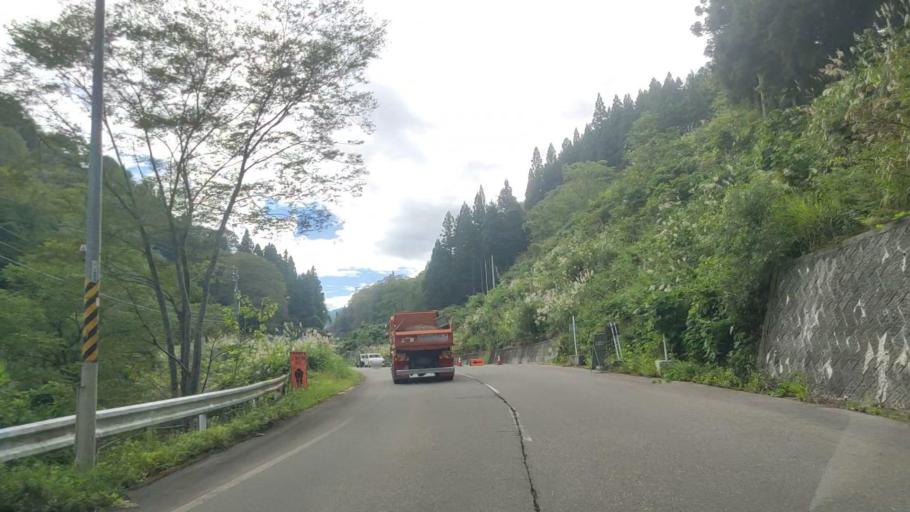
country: JP
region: Nagano
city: Iiyama
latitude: 36.9019
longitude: 138.3177
